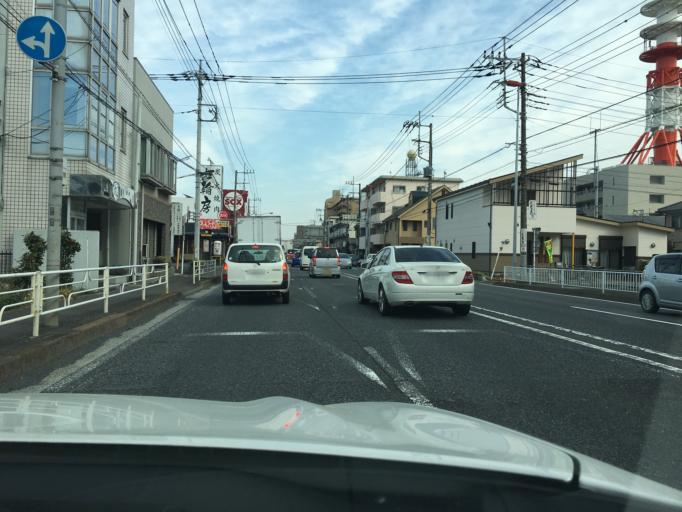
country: JP
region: Saitama
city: Kawagoe
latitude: 35.9018
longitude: 139.4794
